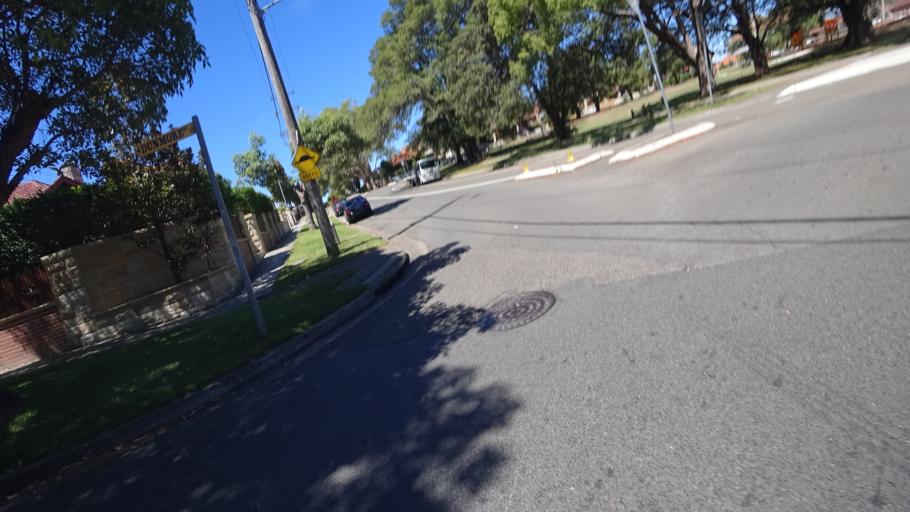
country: AU
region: New South Wales
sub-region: Rockdale
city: Bexley
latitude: -33.9539
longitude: 151.1286
